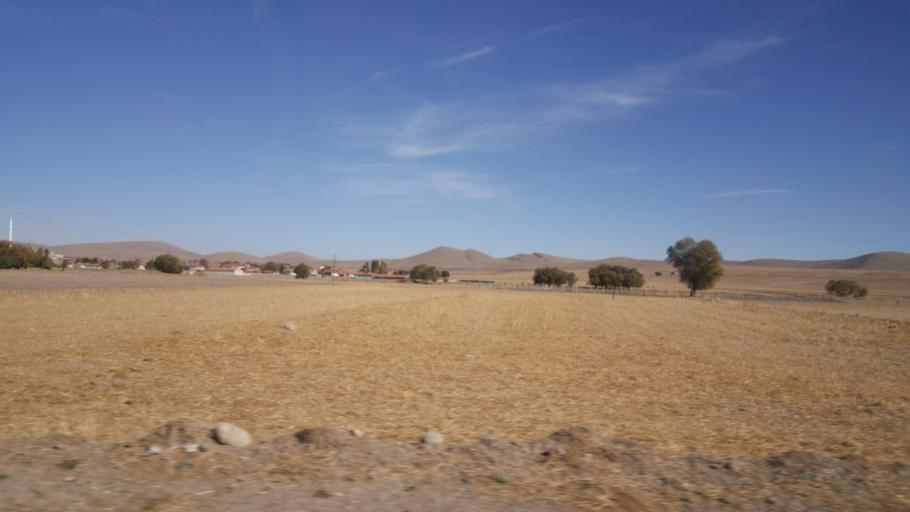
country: TR
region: Ankara
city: Altpinar
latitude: 39.2568
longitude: 32.7523
